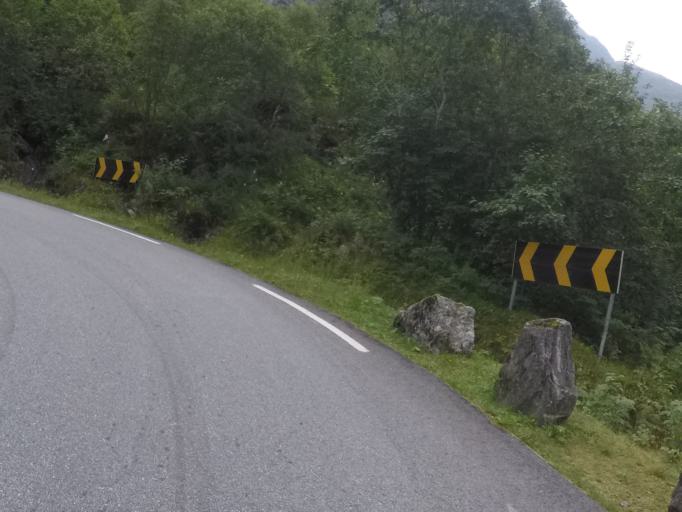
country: NO
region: More og Romsdal
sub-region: Rauma
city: Andalsnes
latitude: 62.4681
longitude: 7.6723
